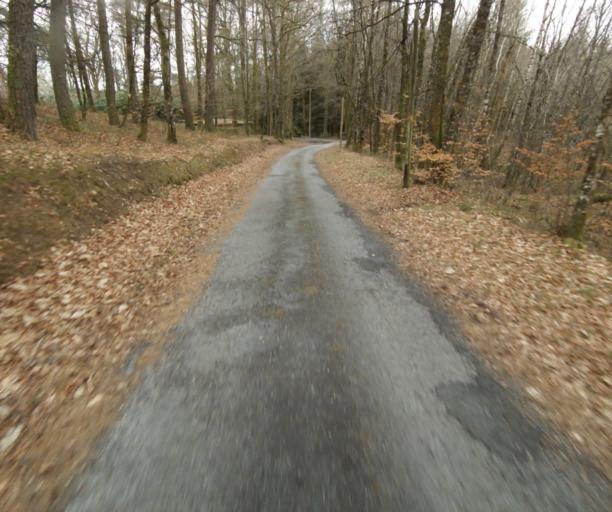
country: FR
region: Limousin
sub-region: Departement de la Correze
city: Correze
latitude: 45.2710
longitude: 1.9491
